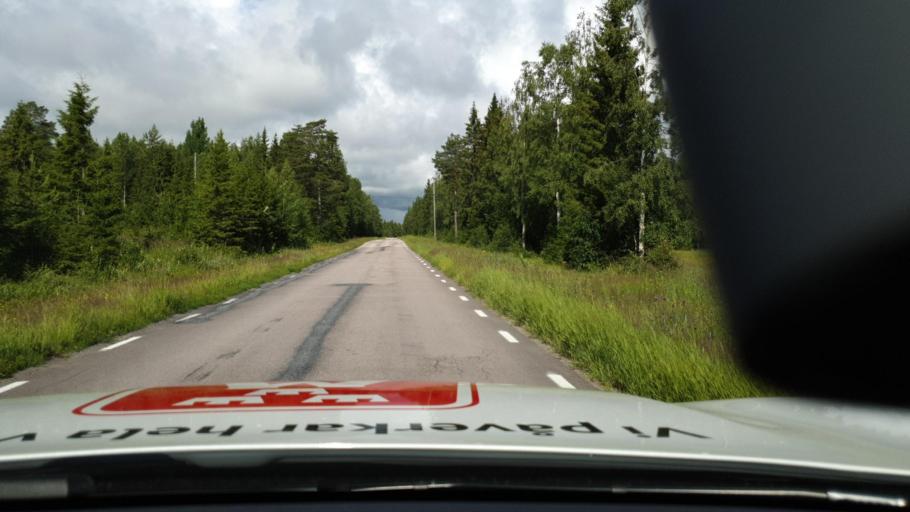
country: SE
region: Norrbotten
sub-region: Lulea Kommun
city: Bergnaset
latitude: 65.4275
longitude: 21.9727
